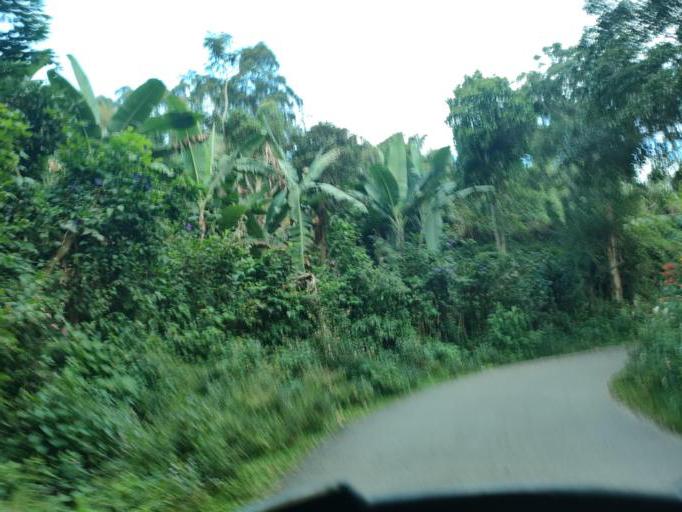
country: IN
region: Tamil Nadu
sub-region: Dindigul
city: Kodaikanal
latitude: 10.2741
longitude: 77.5337
